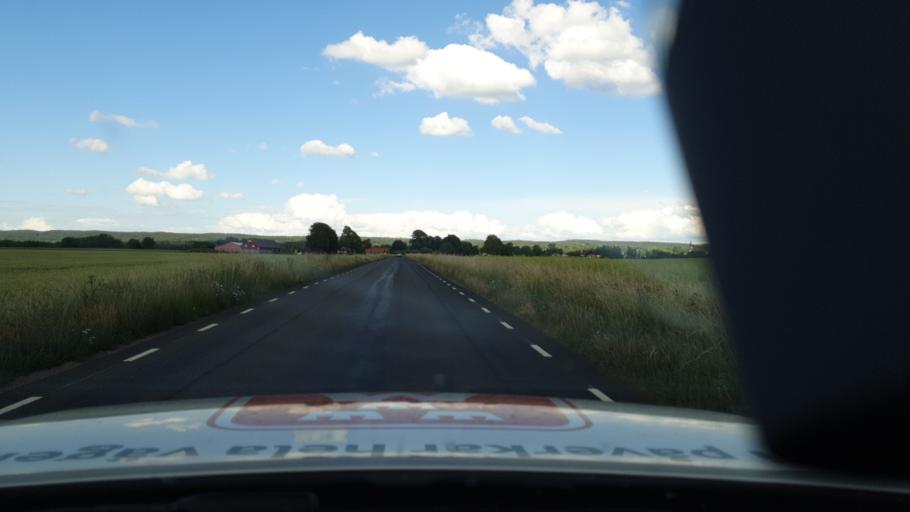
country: SE
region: Vaestra Goetaland
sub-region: Skara Kommun
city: Axvall
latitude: 58.3856
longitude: 13.6274
